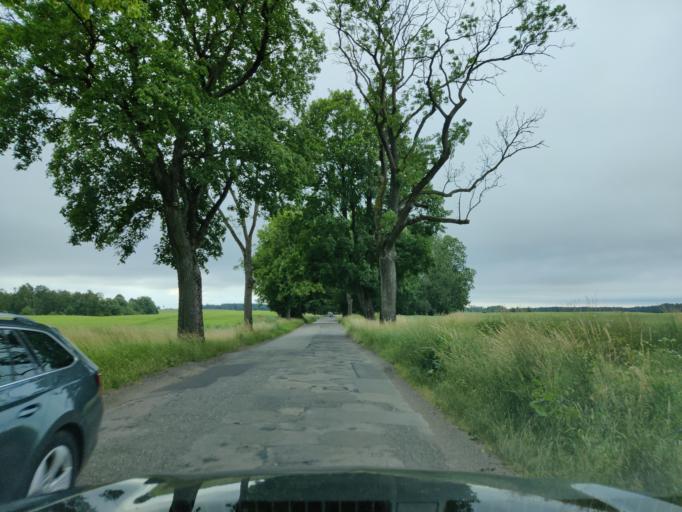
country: PL
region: Warmian-Masurian Voivodeship
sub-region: Powiat gizycki
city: Ryn
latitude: 53.9156
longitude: 21.5570
